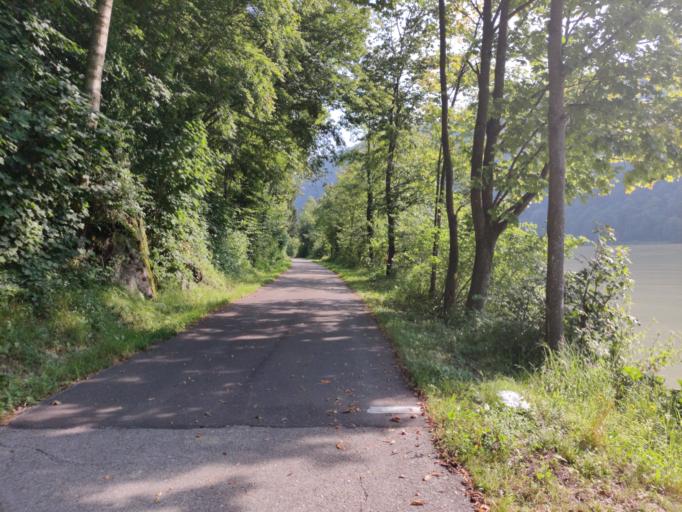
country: AT
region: Upper Austria
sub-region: Politischer Bezirk Rohrbach
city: Kleinzell im Muehlkreis
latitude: 48.4057
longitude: 13.9469
